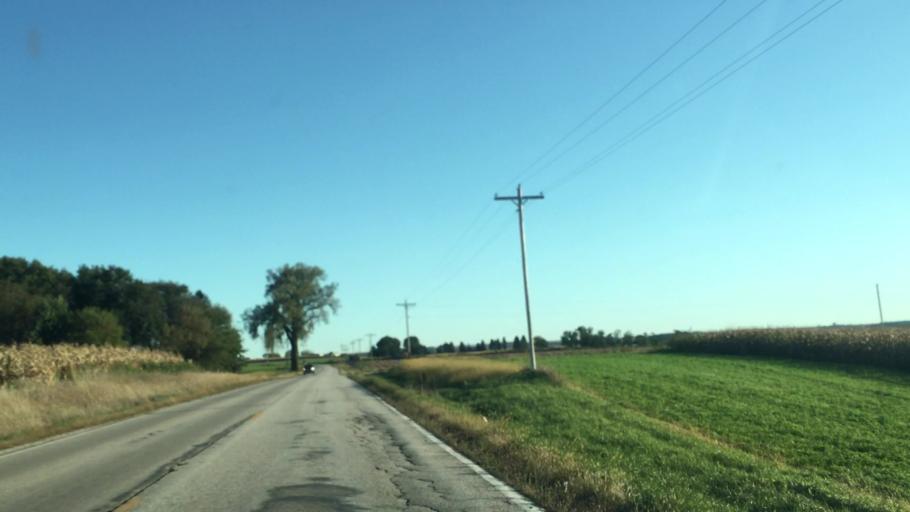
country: US
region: Minnesota
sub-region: Fillmore County
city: Chatfield
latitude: 43.8229
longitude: -92.0692
